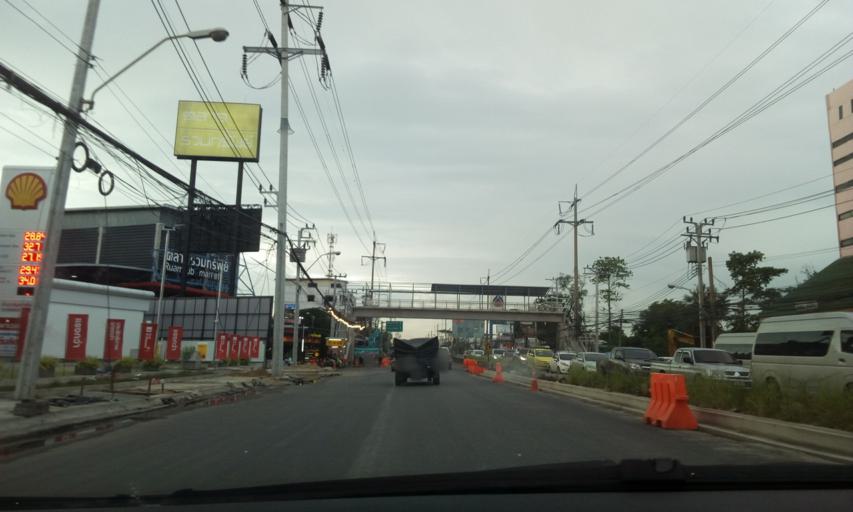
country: TH
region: Nonthaburi
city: Pak Kret
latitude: 13.9436
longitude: 100.5436
